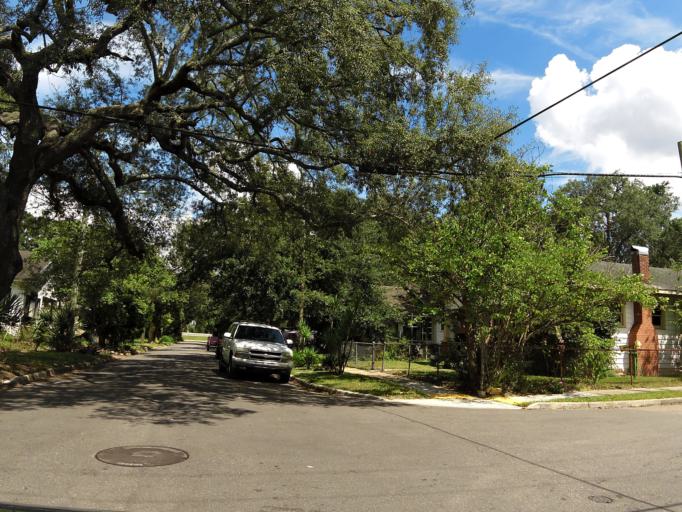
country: US
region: Florida
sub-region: Duval County
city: Jacksonville
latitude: 30.3515
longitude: -81.6389
